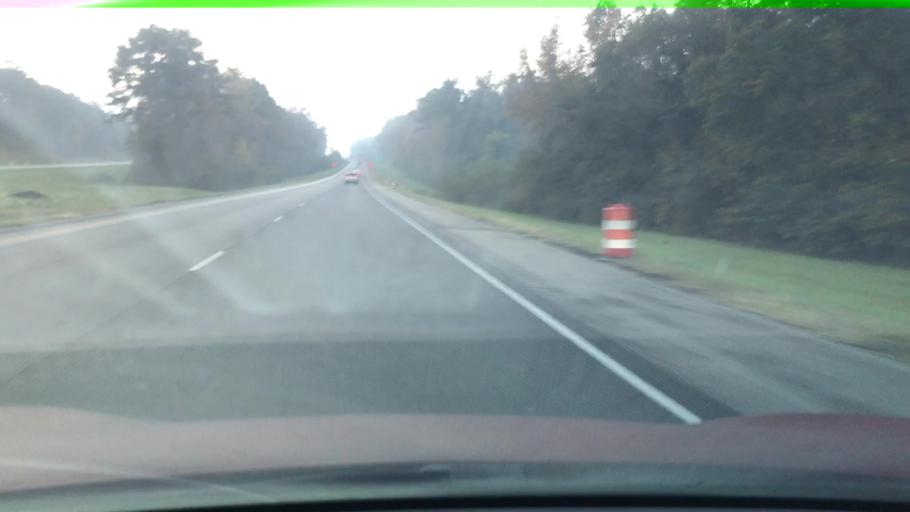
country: US
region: Alabama
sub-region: Chilton County
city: Jemison
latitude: 32.9965
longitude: -86.6998
